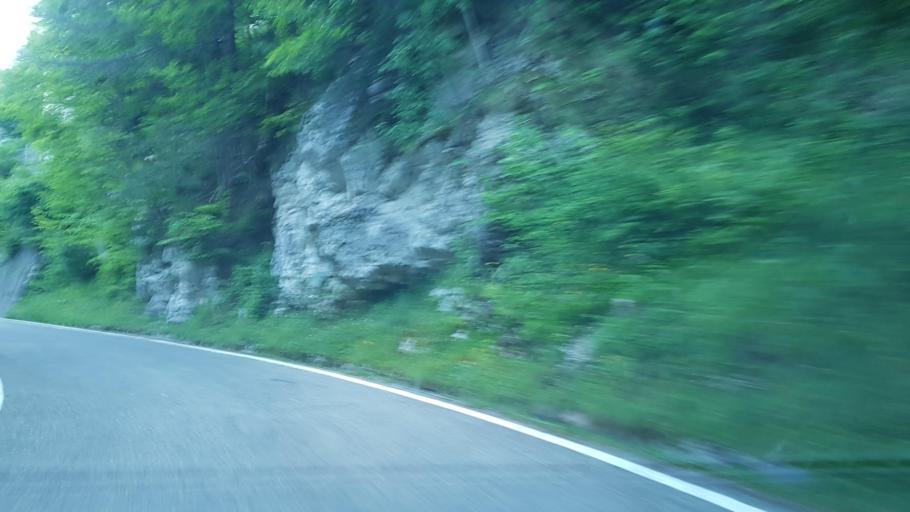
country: IT
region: Friuli Venezia Giulia
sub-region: Provincia di Udine
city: Dogna
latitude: 46.4537
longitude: 13.3608
